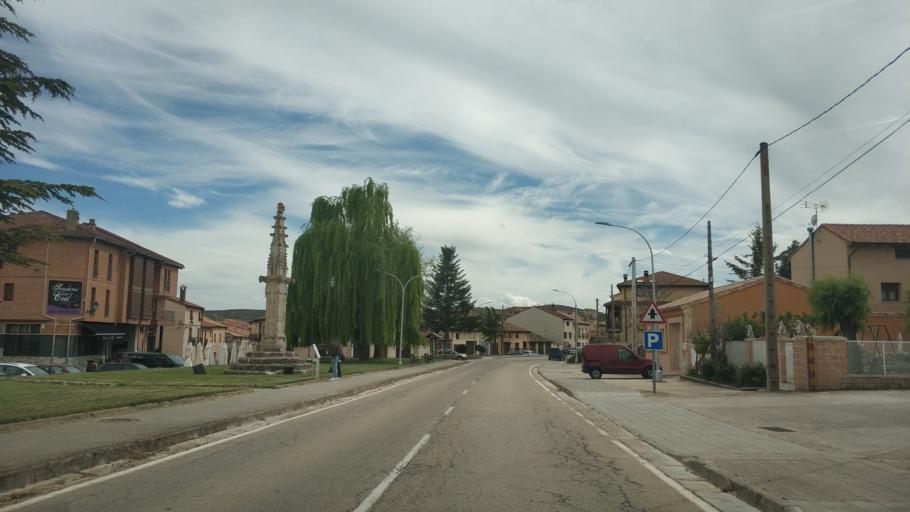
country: ES
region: Castille and Leon
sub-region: Provincia de Soria
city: Berlanga de Duero
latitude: 41.4689
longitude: -2.8619
